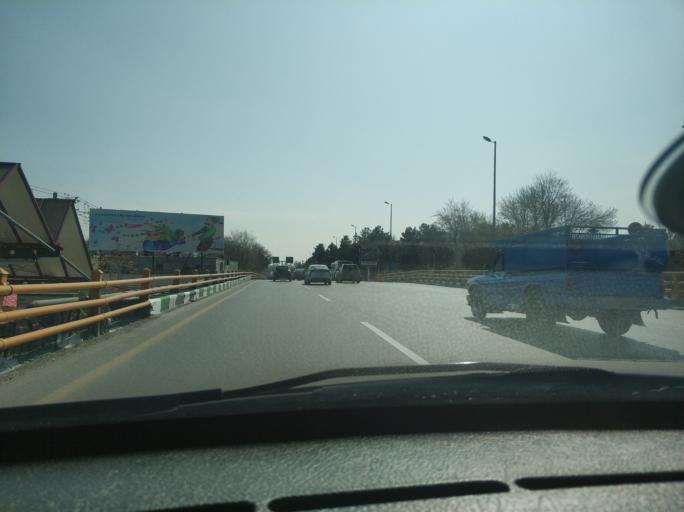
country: IR
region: Razavi Khorasan
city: Mashhad
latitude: 36.3168
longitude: 59.5349
